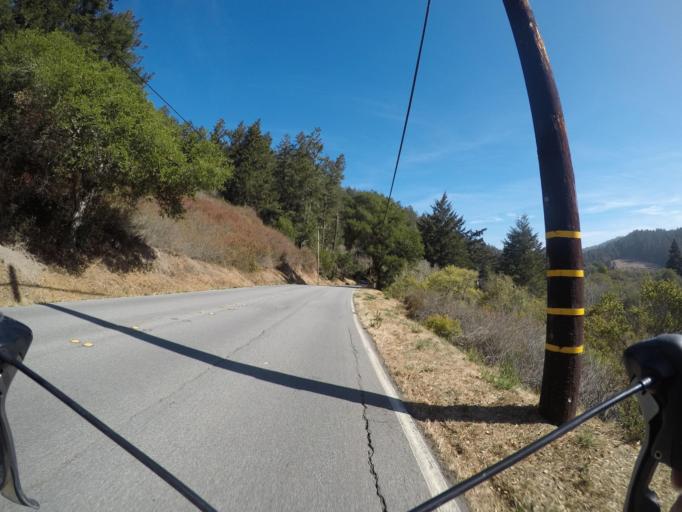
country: US
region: California
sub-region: San Mateo County
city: Portola Valley
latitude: 37.2571
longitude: -122.3423
